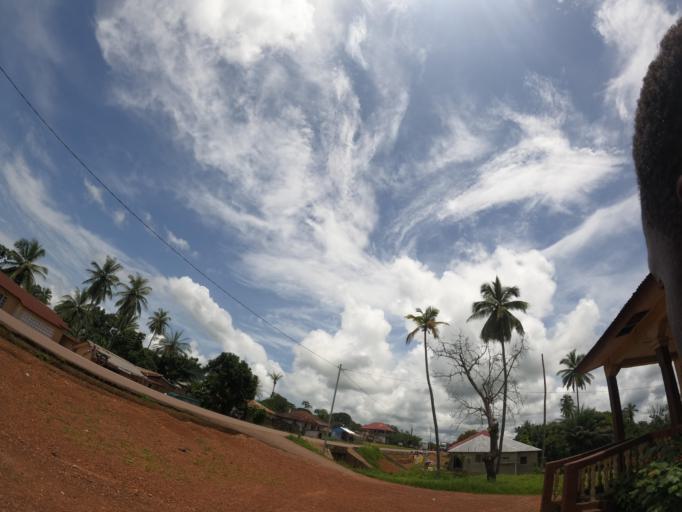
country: SL
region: Northern Province
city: Binkolo
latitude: 9.1068
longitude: -12.2066
